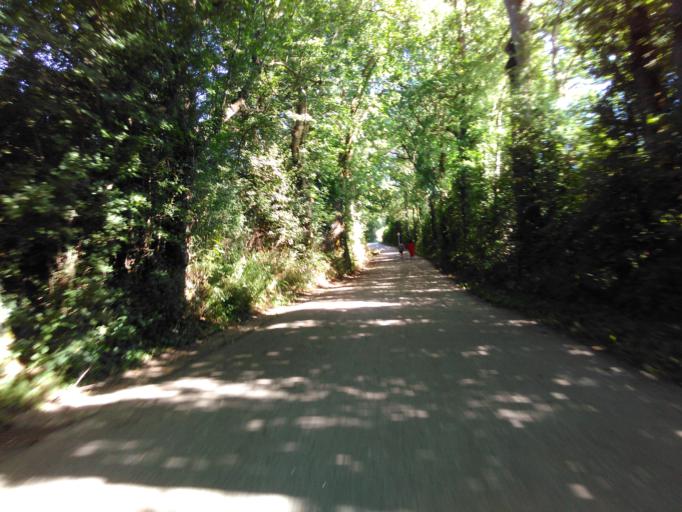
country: LU
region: Luxembourg
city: Soleuvre
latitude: 49.5297
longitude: 5.9315
